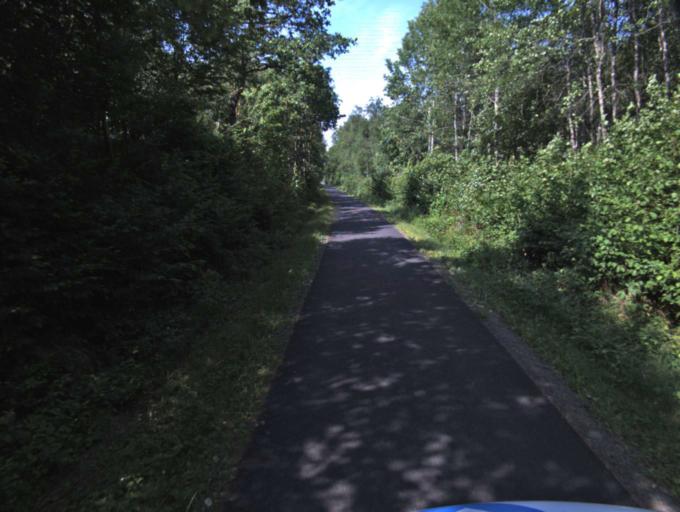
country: SE
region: Skane
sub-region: Kristianstads Kommun
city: Tollarp
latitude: 56.1885
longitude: 14.2879
